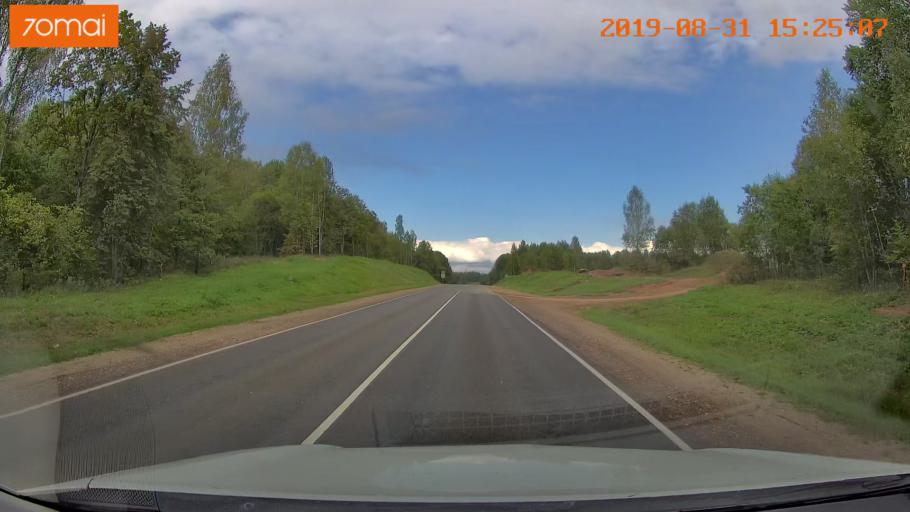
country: RU
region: Kaluga
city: Baryatino
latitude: 54.5371
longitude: 34.5149
